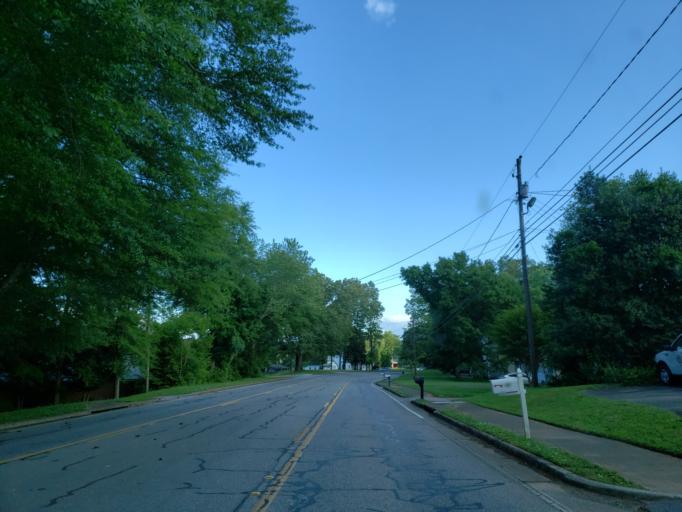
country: US
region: Georgia
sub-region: Cherokee County
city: Canton
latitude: 34.3133
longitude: -84.5548
